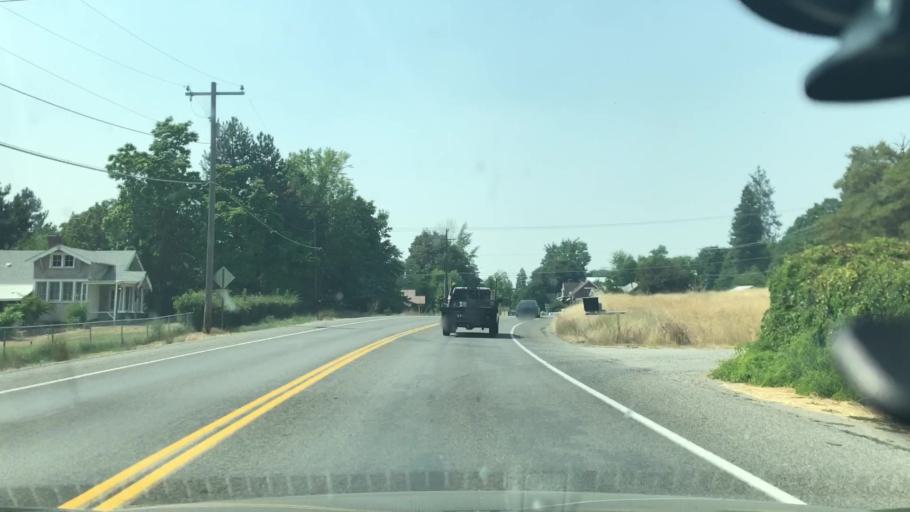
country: US
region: Washington
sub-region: Spokane County
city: Millwood
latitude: 47.6856
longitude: -117.3450
